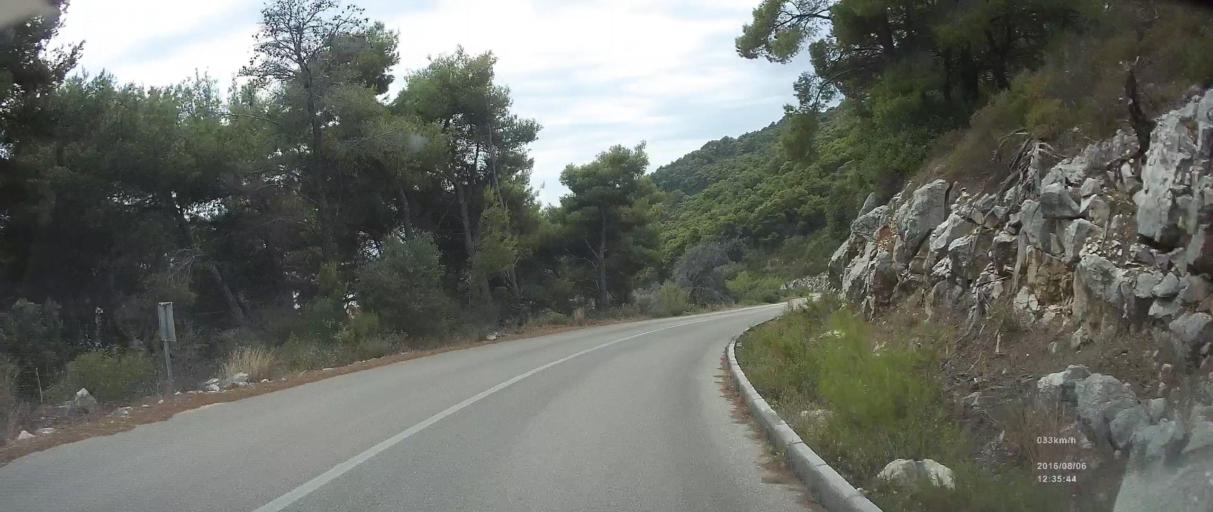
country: HR
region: Dubrovacko-Neretvanska
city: Ston
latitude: 42.7053
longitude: 17.7379
